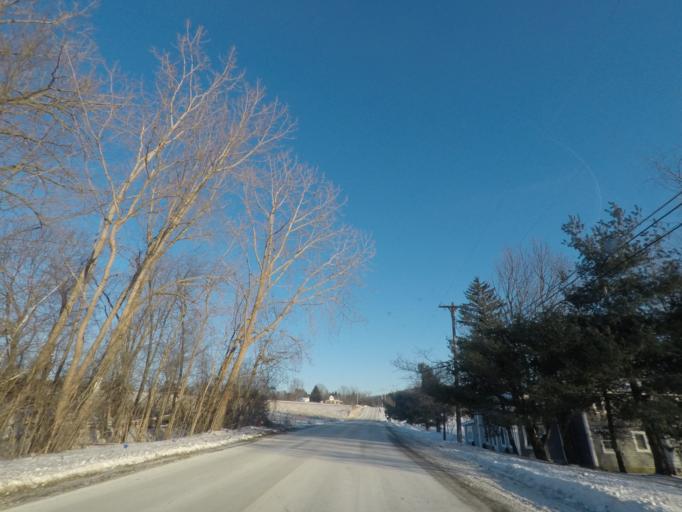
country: US
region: New York
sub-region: Saratoga County
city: Waterford
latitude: 42.8291
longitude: -73.6387
